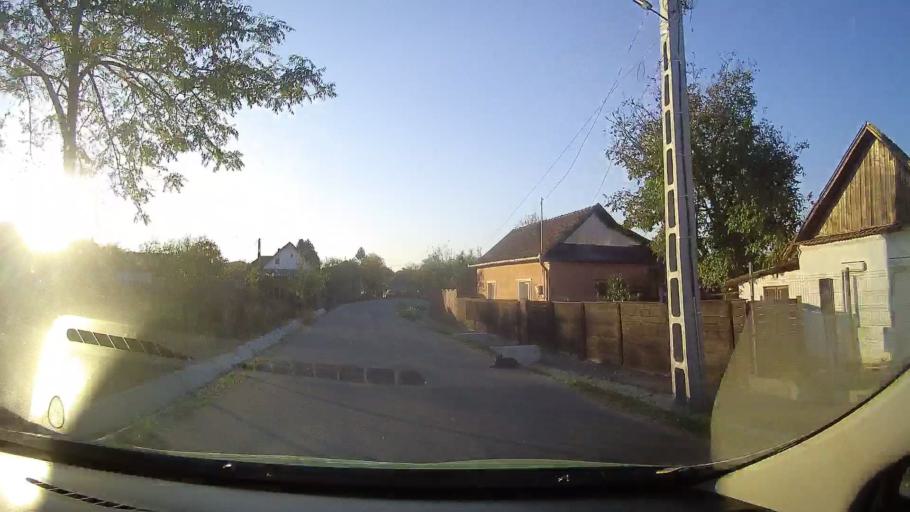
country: RO
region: Bihor
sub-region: Comuna Salard
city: Salard
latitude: 47.2238
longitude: 22.0323
